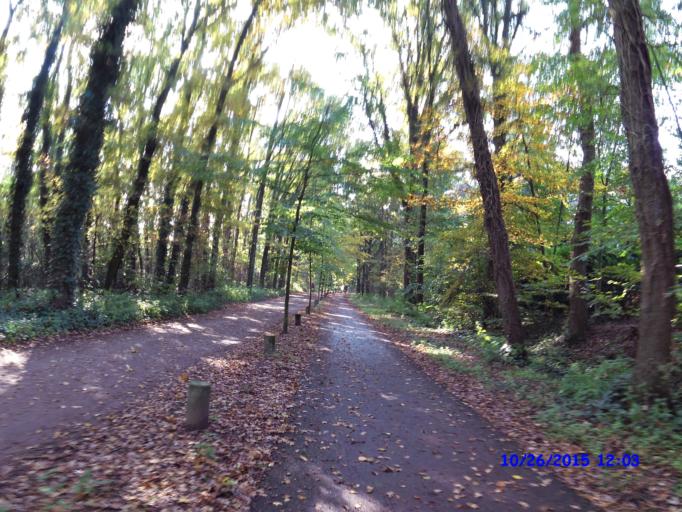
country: NL
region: North Brabant
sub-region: Gemeente Geldrop-Mierlo
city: Mierlo
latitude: 51.4354
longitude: 5.6135
